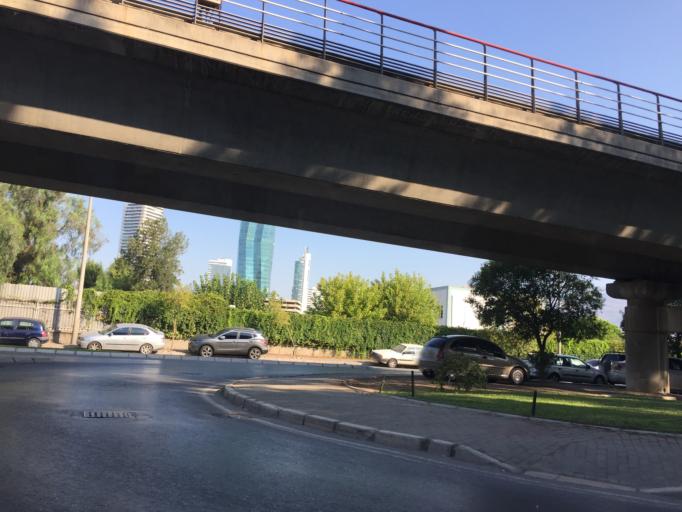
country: TR
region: Izmir
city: Buca
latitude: 38.4434
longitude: 27.1825
